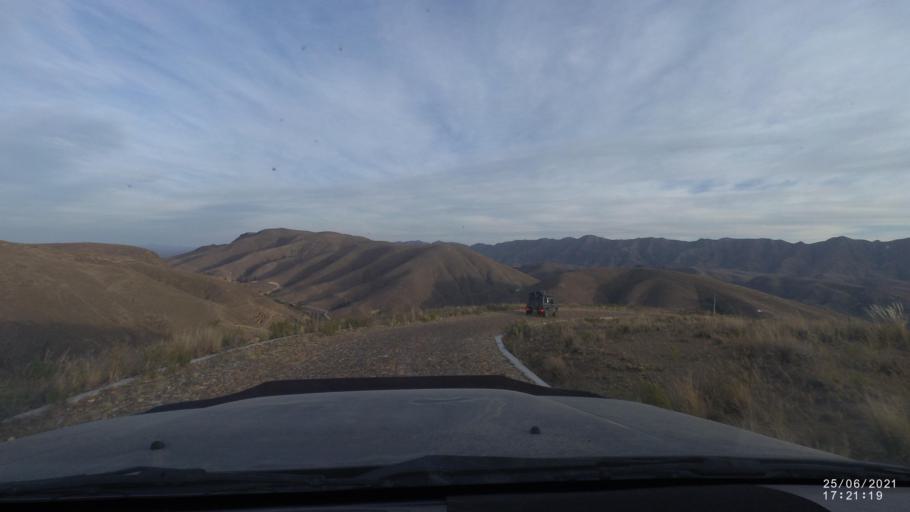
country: BO
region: Cochabamba
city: Mizque
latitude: -17.9081
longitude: -65.6864
